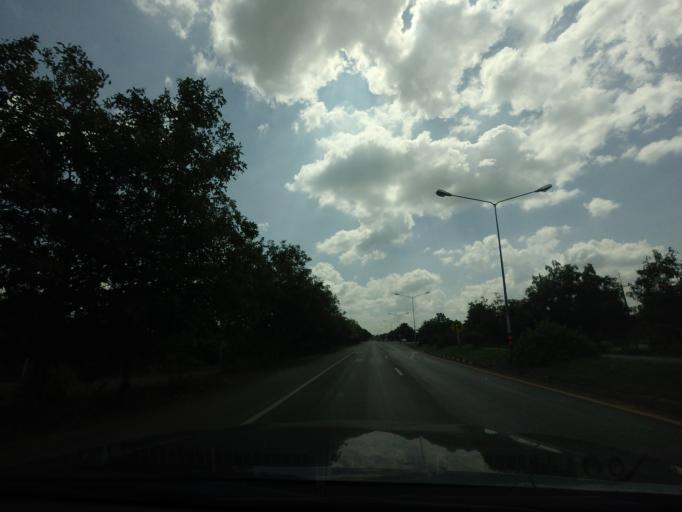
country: TH
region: Phetchabun
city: Nong Phai
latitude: 16.1269
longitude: 101.0418
